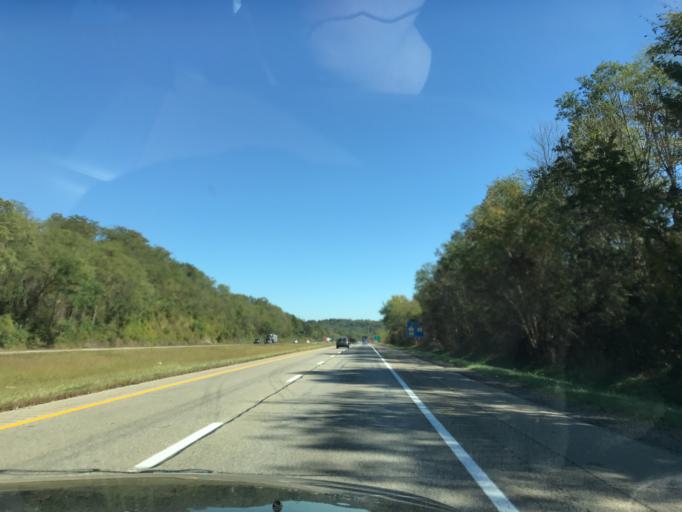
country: US
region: Ohio
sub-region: Muskingum County
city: Zanesville
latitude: 39.9471
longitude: -82.0670
